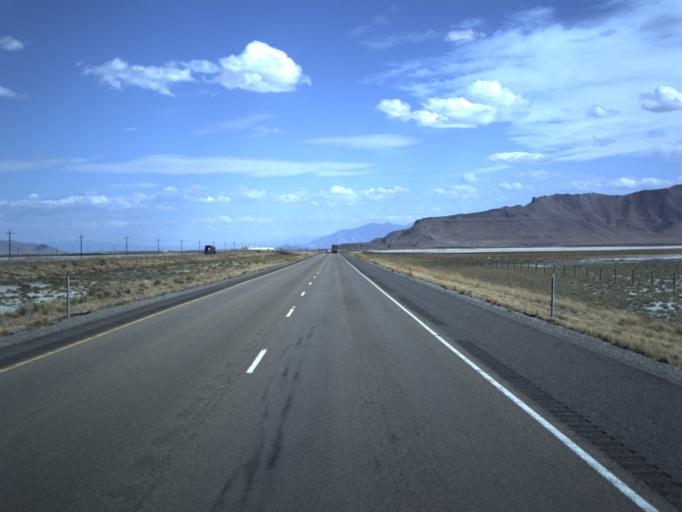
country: US
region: Utah
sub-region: Tooele County
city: Grantsville
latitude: 40.7519
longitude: -112.7161
